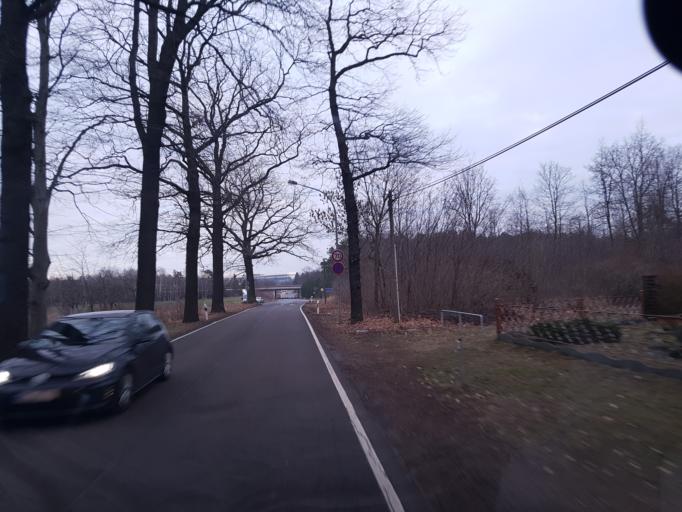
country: DE
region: Brandenburg
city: Schipkau
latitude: 51.5372
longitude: 13.9046
